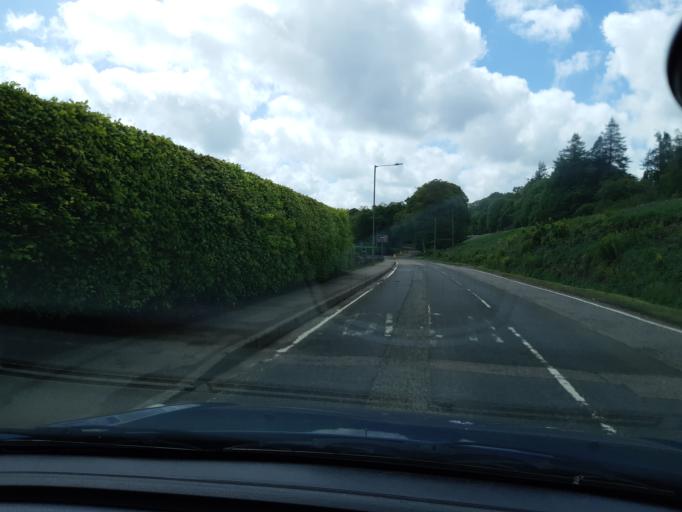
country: GB
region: Scotland
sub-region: Argyll and Bute
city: Lochgilphead
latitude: 56.0385
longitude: -5.4411
